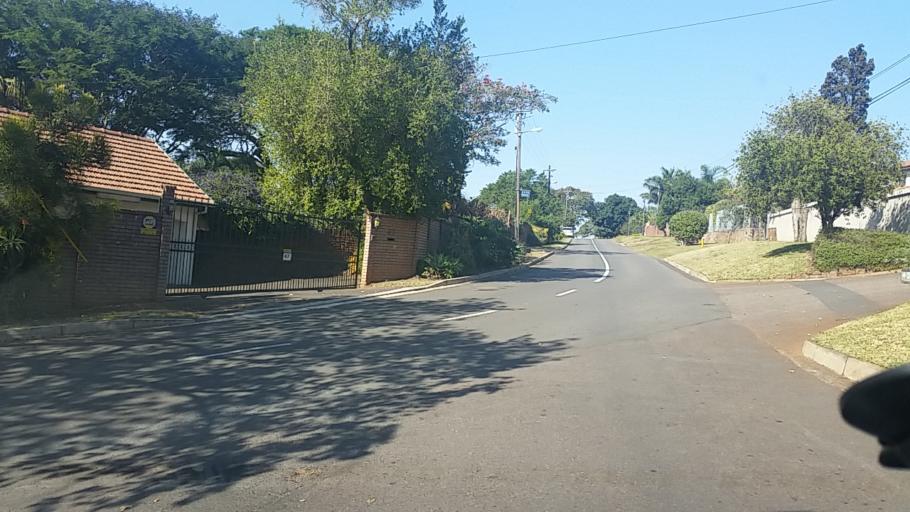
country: ZA
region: KwaZulu-Natal
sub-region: eThekwini Metropolitan Municipality
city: Berea
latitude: -29.8516
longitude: 30.9005
